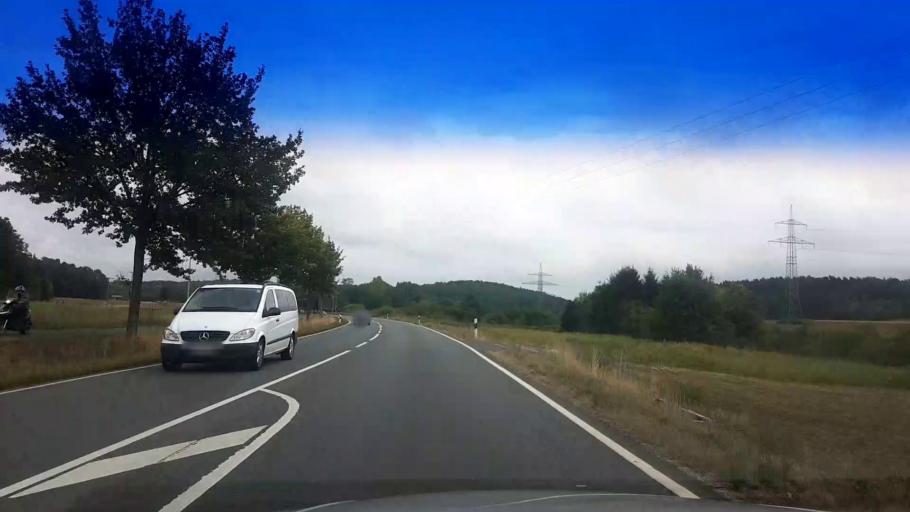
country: DE
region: Bavaria
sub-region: Upper Franconia
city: Heroldsbach
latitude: 49.7036
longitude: 11.0136
